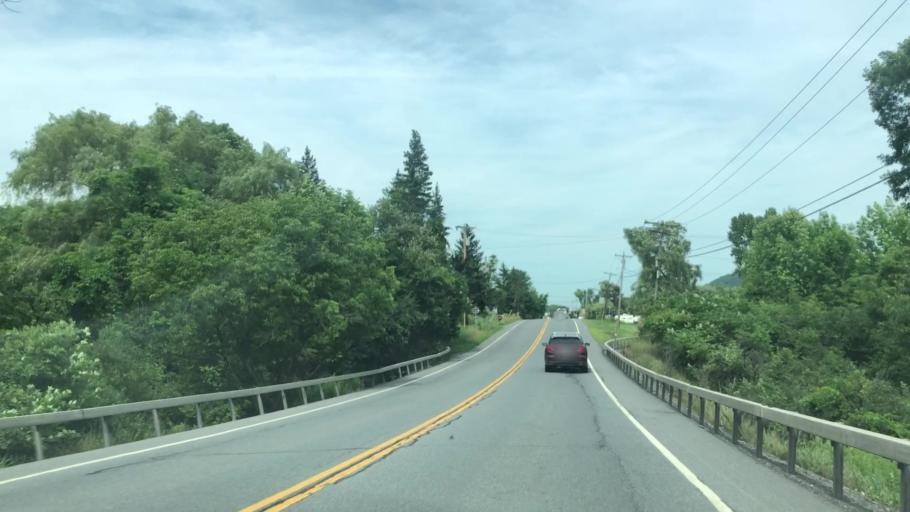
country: US
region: New York
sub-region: Washington County
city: Whitehall
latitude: 43.5343
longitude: -73.4106
